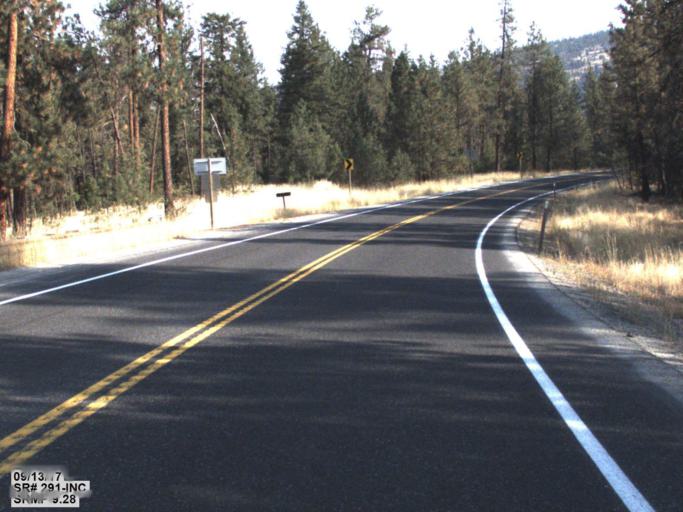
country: US
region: Washington
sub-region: Spokane County
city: Fairwood
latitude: 47.7781
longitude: -117.5440
